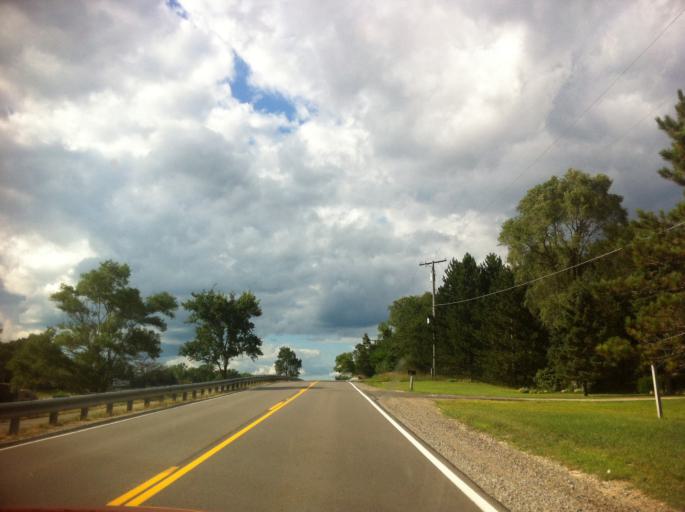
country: US
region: Michigan
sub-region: Livingston County
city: Whitmore Lake
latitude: 42.4820
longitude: -83.7558
